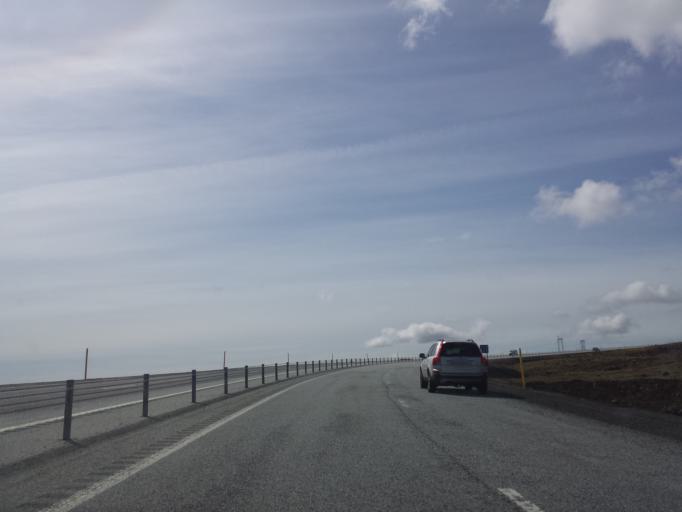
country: IS
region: South
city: Hveragerdi
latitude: 64.0124
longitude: -21.2345
